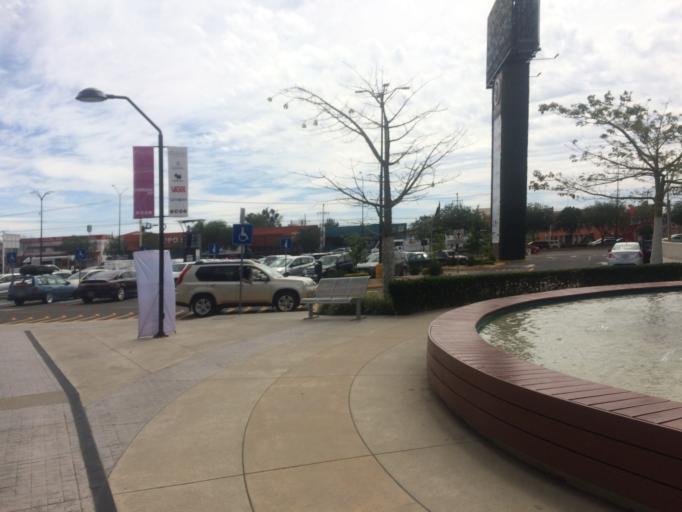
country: MX
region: Guanajuato
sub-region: Leon
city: Fraccionamiento Paraiso Real
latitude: 21.0874
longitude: -101.6157
